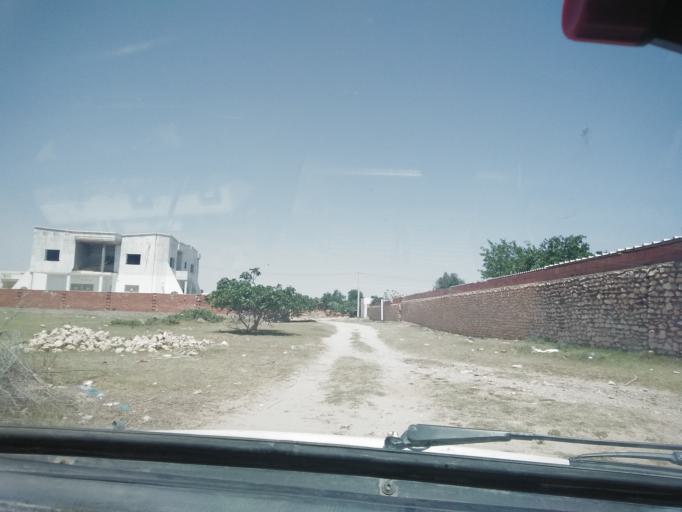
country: TN
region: Safaqis
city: Al Qarmadah
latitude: 34.8050
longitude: 10.7757
